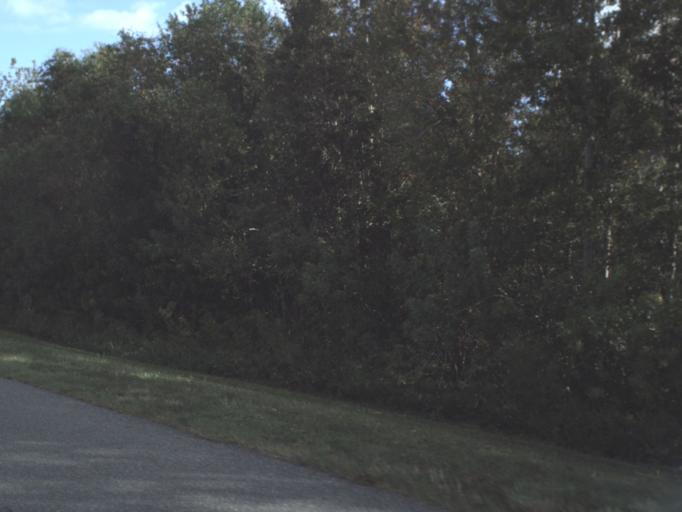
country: US
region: Florida
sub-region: Orange County
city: Southchase
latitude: 28.4177
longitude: -81.3921
